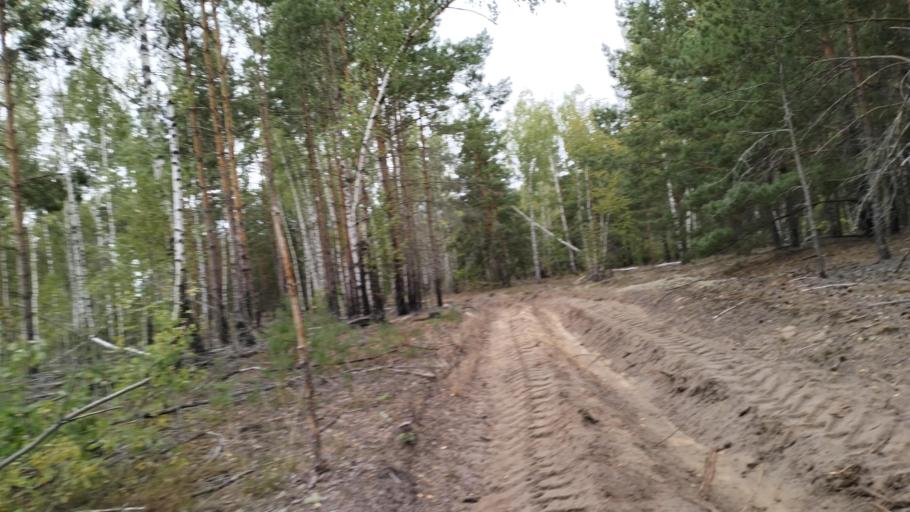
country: BY
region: Brest
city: Davyd-Haradok
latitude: 51.8768
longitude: 27.2119
